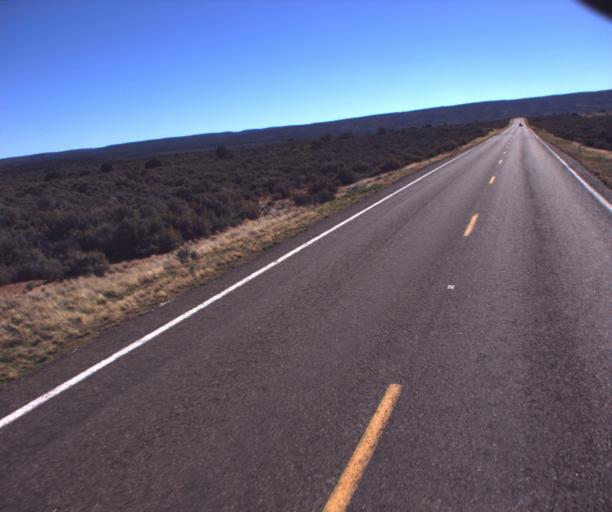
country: US
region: Arizona
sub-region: Coconino County
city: Fredonia
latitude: 36.8644
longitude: -112.3161
